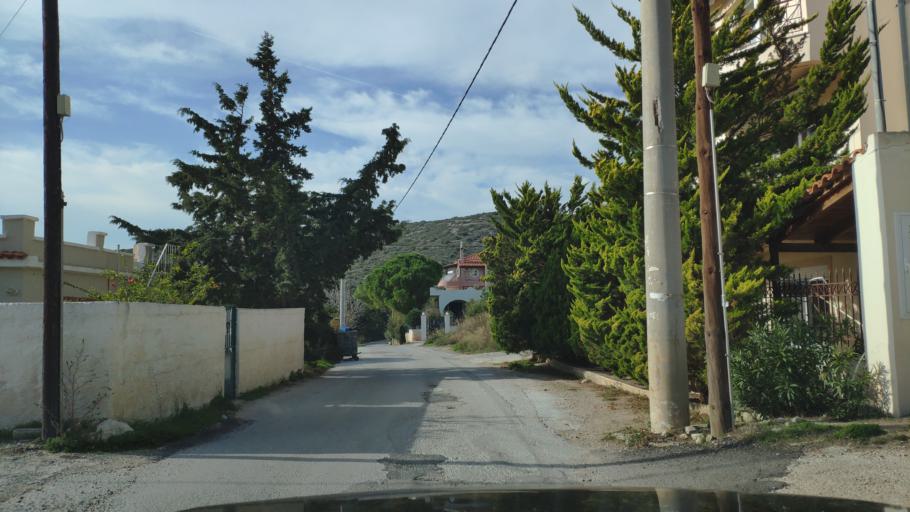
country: GR
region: Attica
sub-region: Nomarchia Anatolikis Attikis
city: Limin Mesoyaias
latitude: 37.8999
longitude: 24.0255
